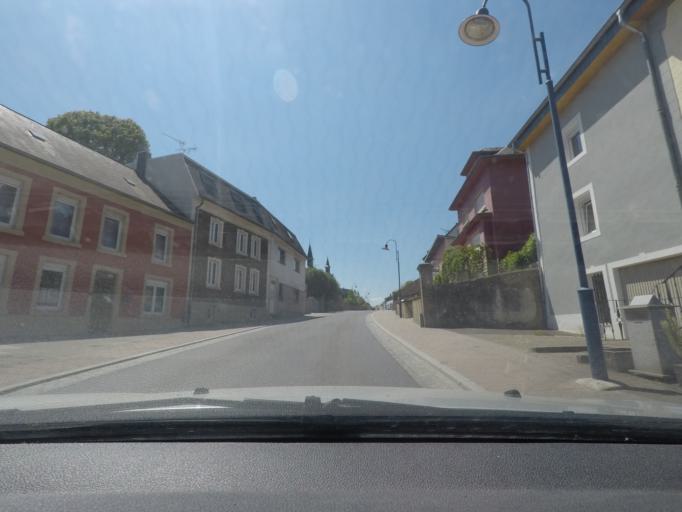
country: LU
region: Diekirch
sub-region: Canton de Redange
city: Redange-sur-Attert
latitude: 49.7656
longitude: 5.8921
